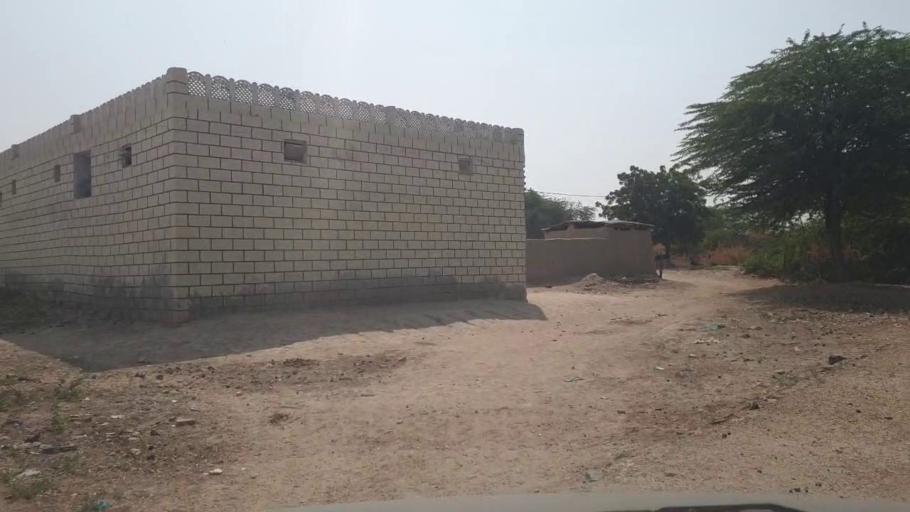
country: PK
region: Sindh
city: Chor
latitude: 25.4744
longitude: 69.7748
